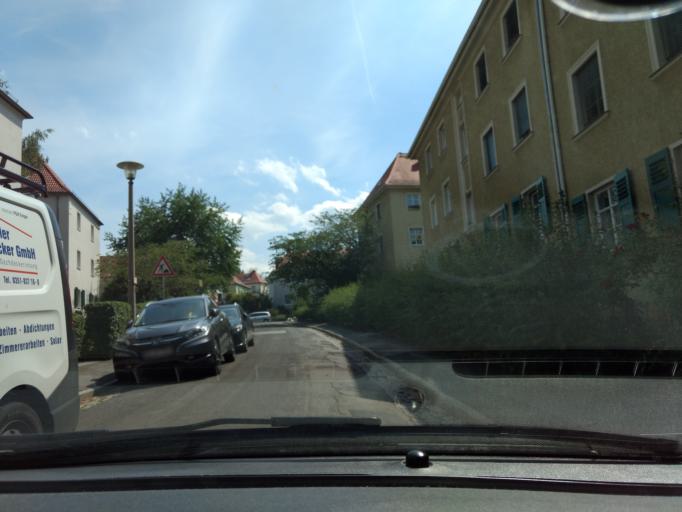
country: DE
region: Saxony
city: Dresden
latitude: 51.0274
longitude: 13.7341
